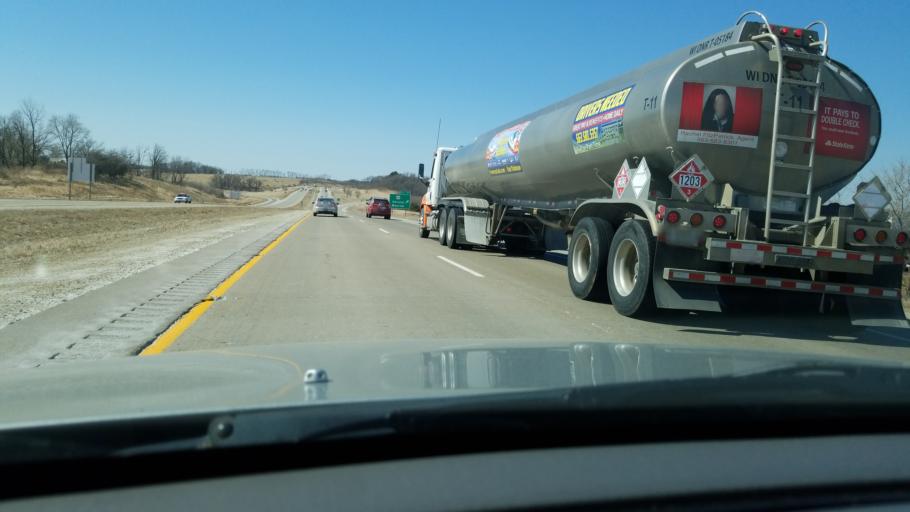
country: US
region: Wisconsin
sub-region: Dane County
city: Verona
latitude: 42.9736
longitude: -89.5361
